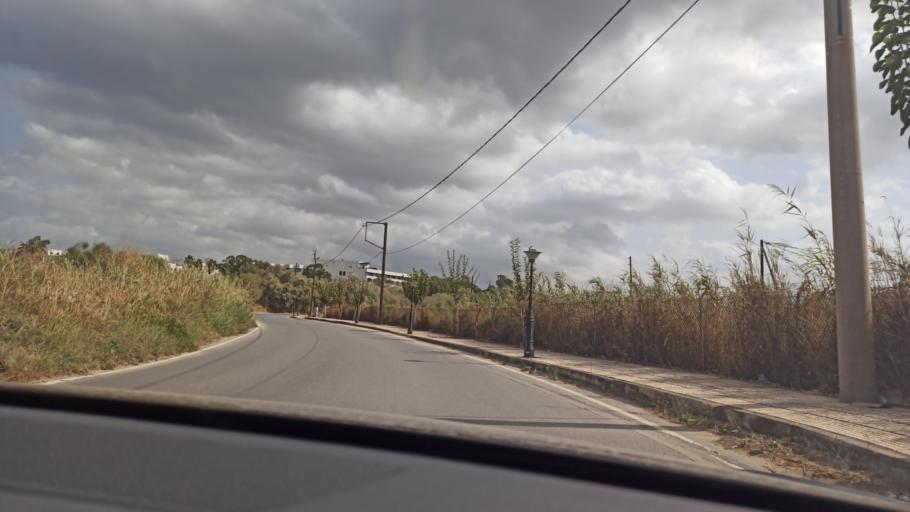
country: GR
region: Crete
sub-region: Nomos Irakleiou
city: Gazi
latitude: 35.3395
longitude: 25.0541
